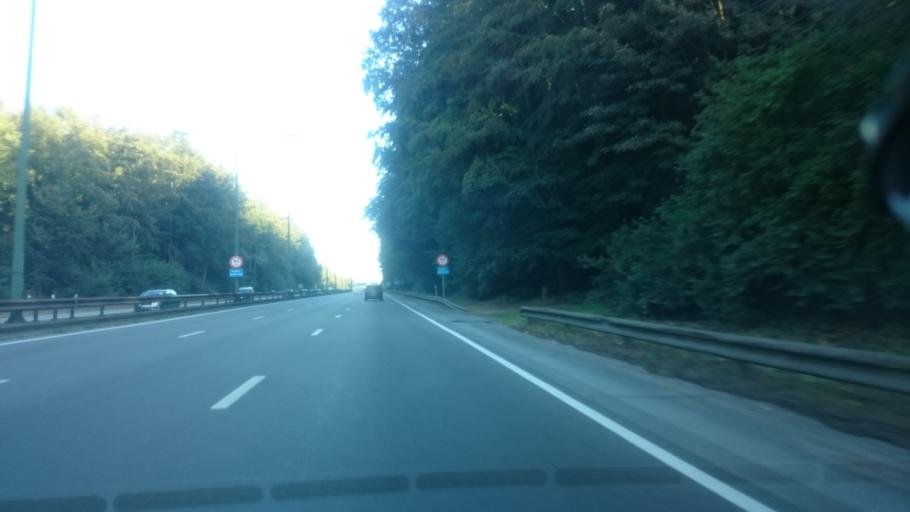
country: BE
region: Flanders
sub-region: Provincie Vlaams-Brabant
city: Hoeilaart
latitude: 50.8059
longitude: 4.4530
